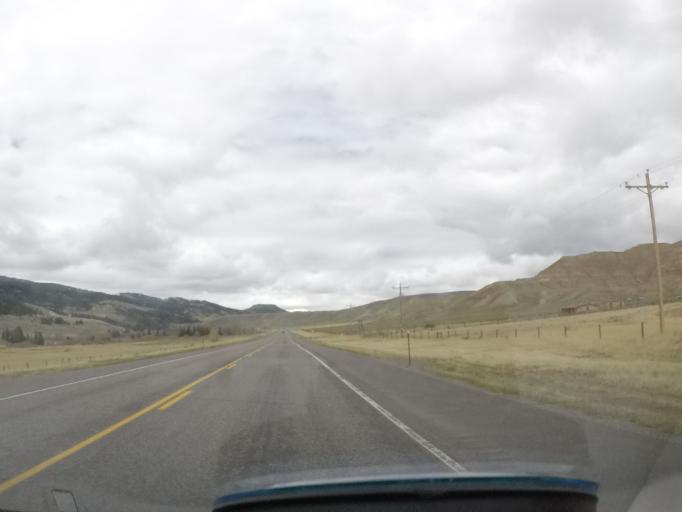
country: US
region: Wyoming
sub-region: Sublette County
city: Pinedale
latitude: 43.5733
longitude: -109.7265
